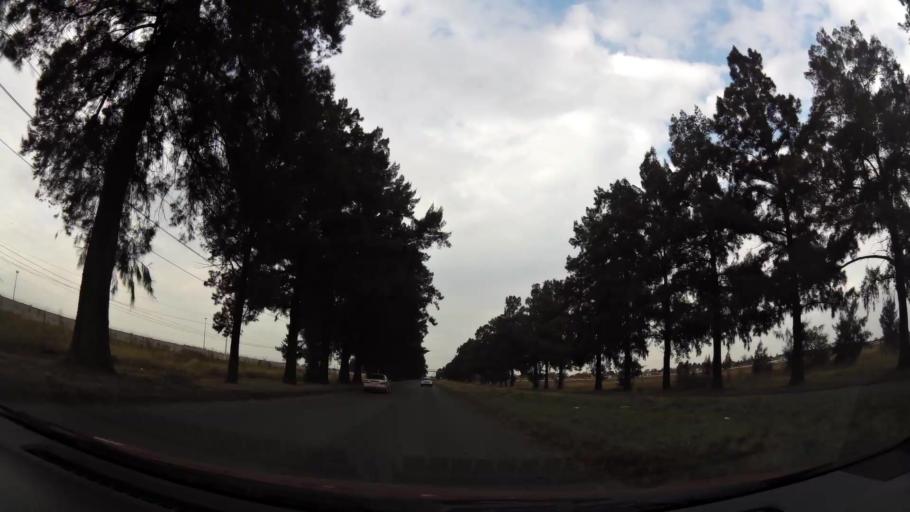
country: ZA
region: Gauteng
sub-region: Sedibeng District Municipality
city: Vanderbijlpark
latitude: -26.6740
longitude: 27.8263
